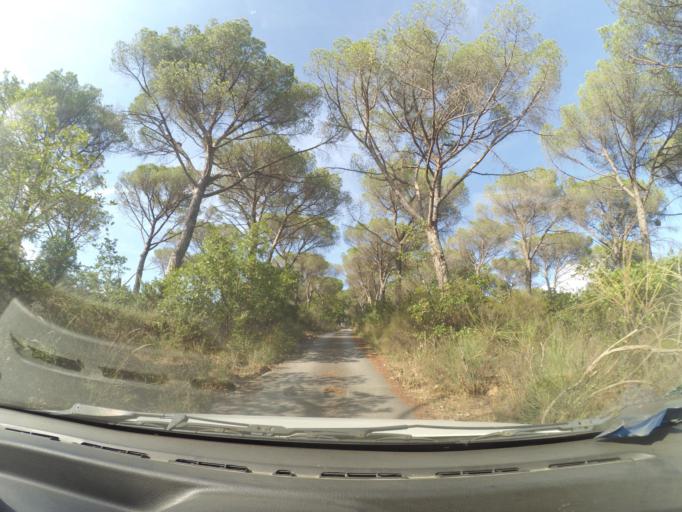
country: IT
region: Tuscany
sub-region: Province of Arezzo
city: Castiglion Fibocchi
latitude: 43.5305
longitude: 11.7820
